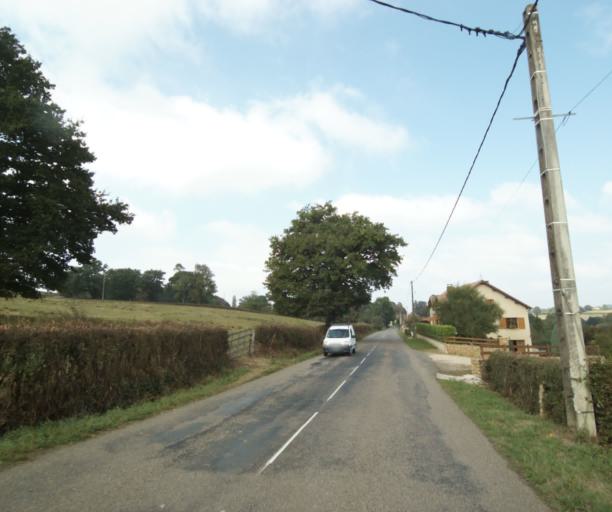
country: FR
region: Bourgogne
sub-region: Departement de Saone-et-Loire
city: Charolles
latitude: 46.4293
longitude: 4.3009
